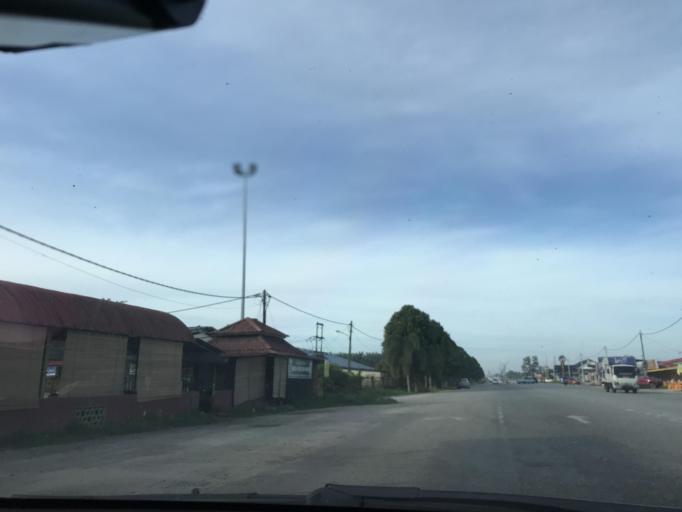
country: MY
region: Kelantan
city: Tanah Merah
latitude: 5.8198
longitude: 102.1489
